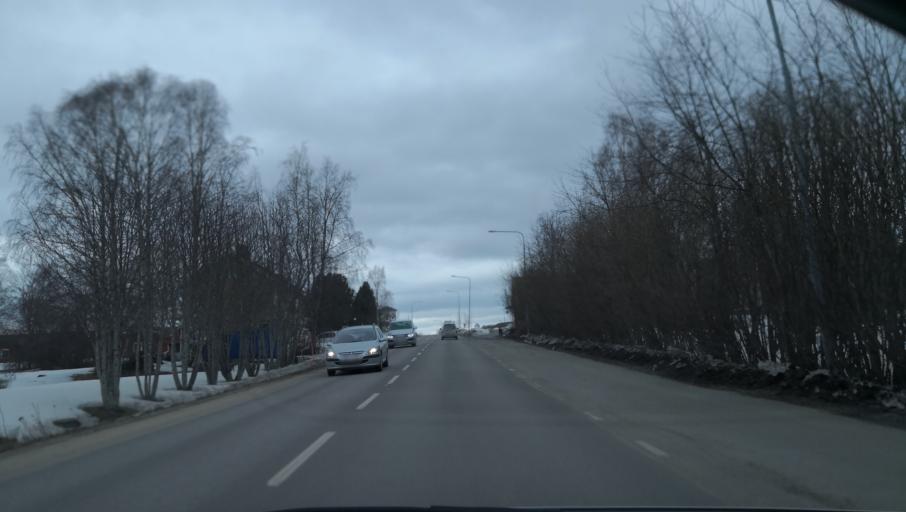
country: SE
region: Vaesterbotten
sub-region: Vannas Kommun
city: Vannasby
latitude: 63.9150
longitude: 19.8082
